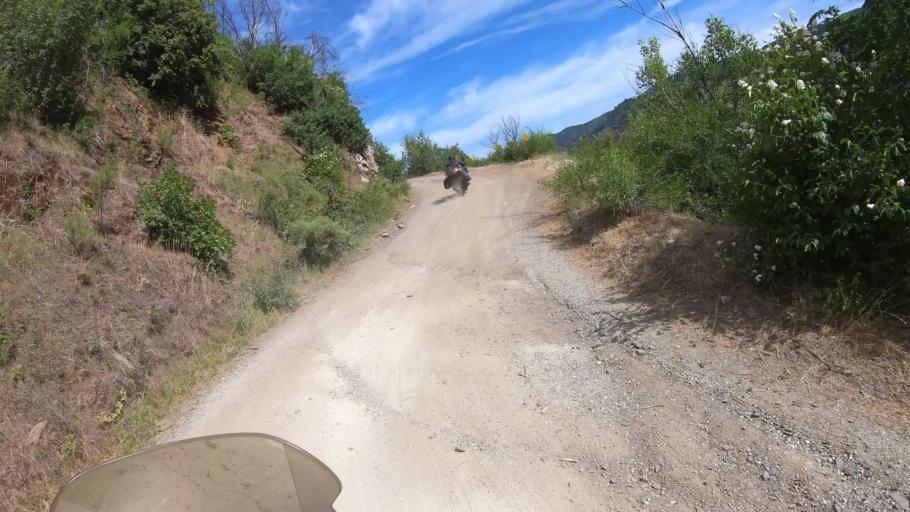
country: US
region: California
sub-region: Tuolumne County
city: Tuolumne City
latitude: 37.8315
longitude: -120.0971
